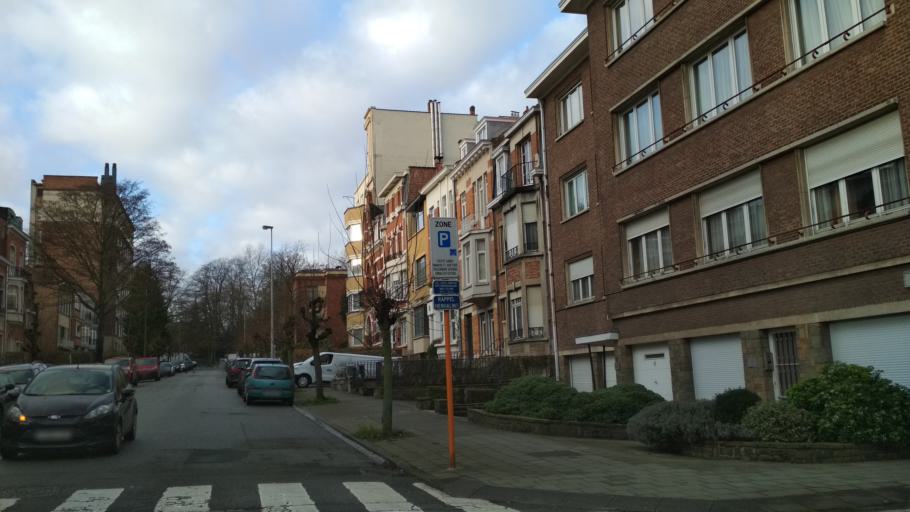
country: BE
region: Flanders
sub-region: Provincie Vlaams-Brabant
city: Diegem
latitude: 50.8410
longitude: 4.4099
